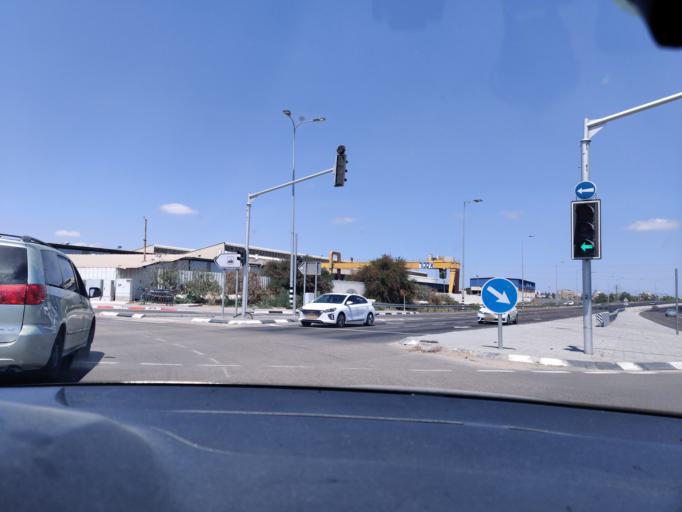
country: IL
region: Southern District
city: Qiryat Gat
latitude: 31.6084
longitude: 34.7868
